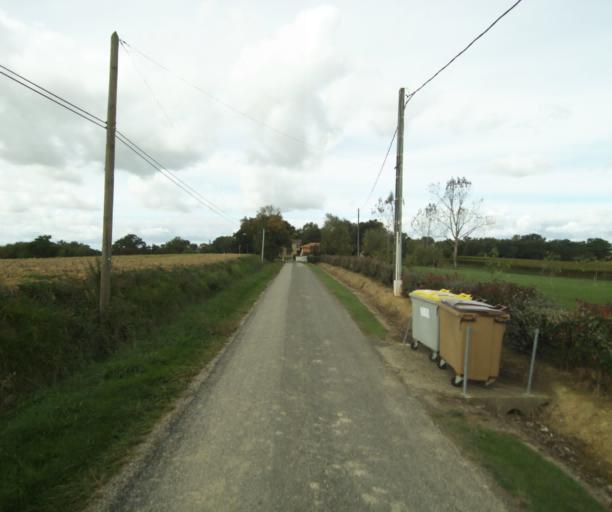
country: FR
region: Midi-Pyrenees
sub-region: Departement du Gers
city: Eauze
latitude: 43.8434
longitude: 0.0893
